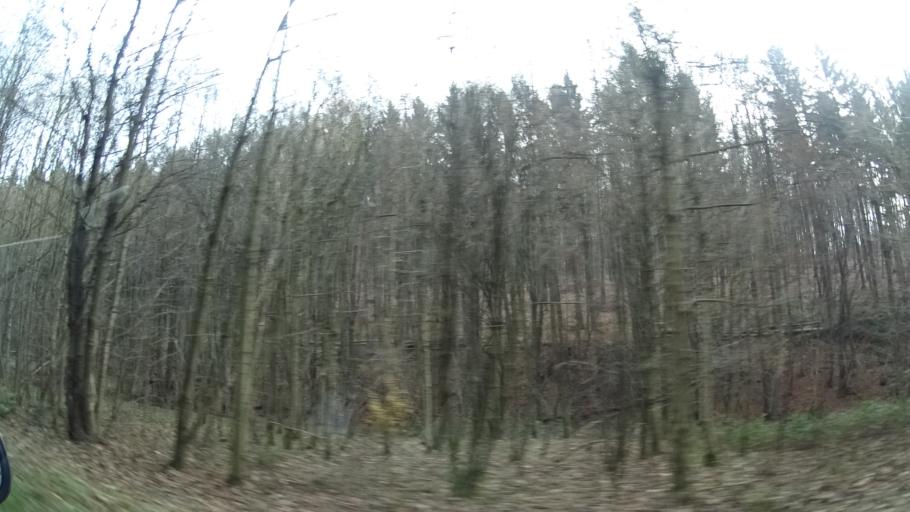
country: DE
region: Baden-Wuerttemberg
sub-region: Karlsruhe Region
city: Reichartshausen
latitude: 49.3849
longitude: 8.9121
